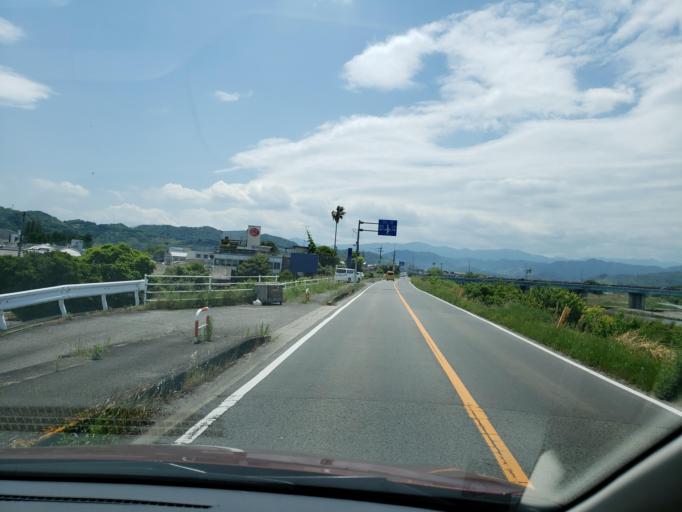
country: JP
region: Tokushima
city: Tokushima-shi
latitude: 34.0749
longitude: 134.5012
